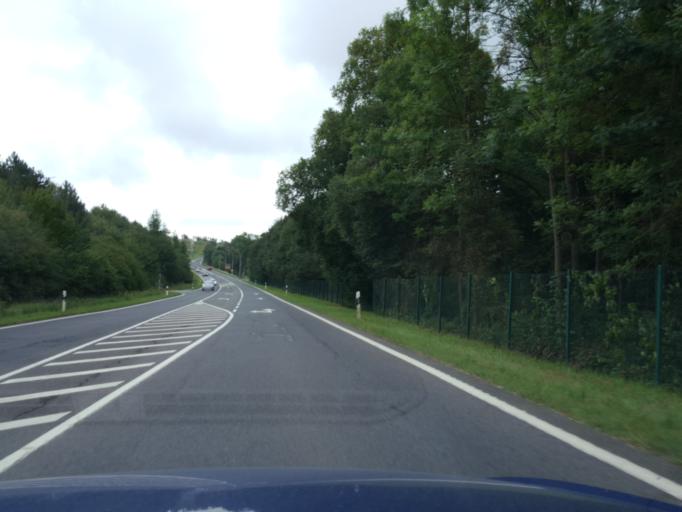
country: LU
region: Luxembourg
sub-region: Canton de Mersch
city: Mersch
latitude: 49.7678
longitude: 6.0874
